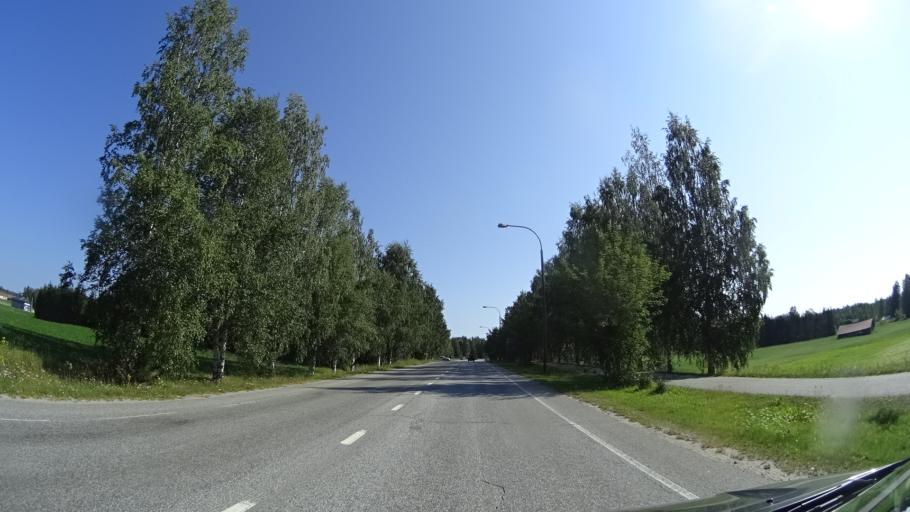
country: FI
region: North Karelia
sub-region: Joensuu
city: Juuka
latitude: 63.2457
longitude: 29.2626
